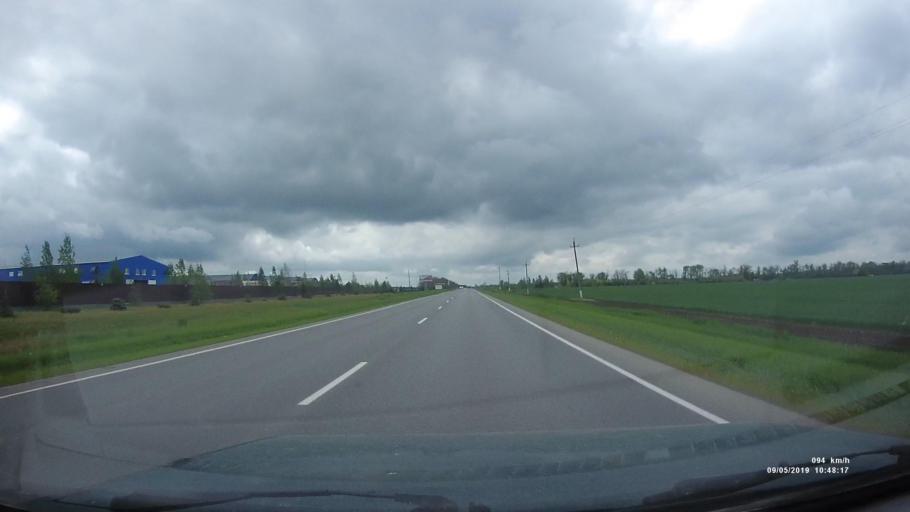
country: RU
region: Rostov
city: Peshkovo
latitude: 46.9588
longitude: 39.3561
